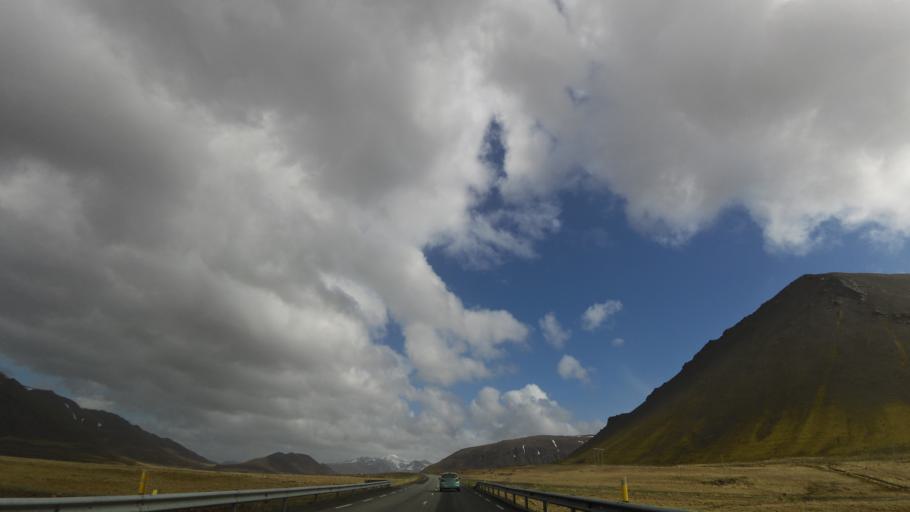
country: IS
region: West
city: Stykkisholmur
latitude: 64.9611
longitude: -23.0917
